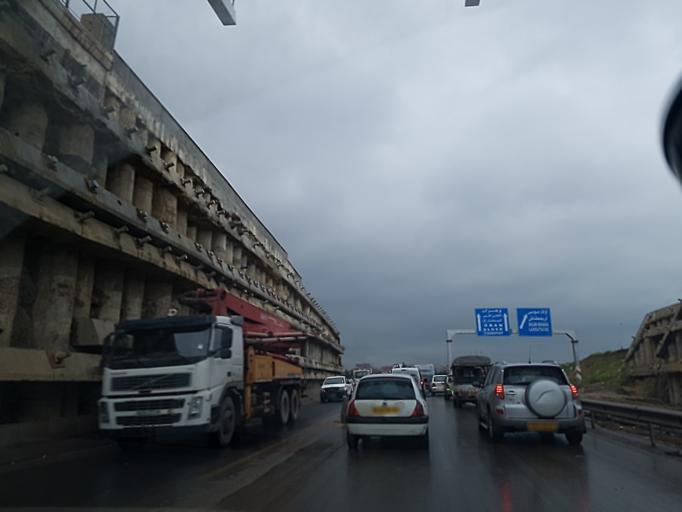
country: DZ
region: Boumerdes
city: Ouled Moussa
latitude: 36.6755
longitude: 3.3776
